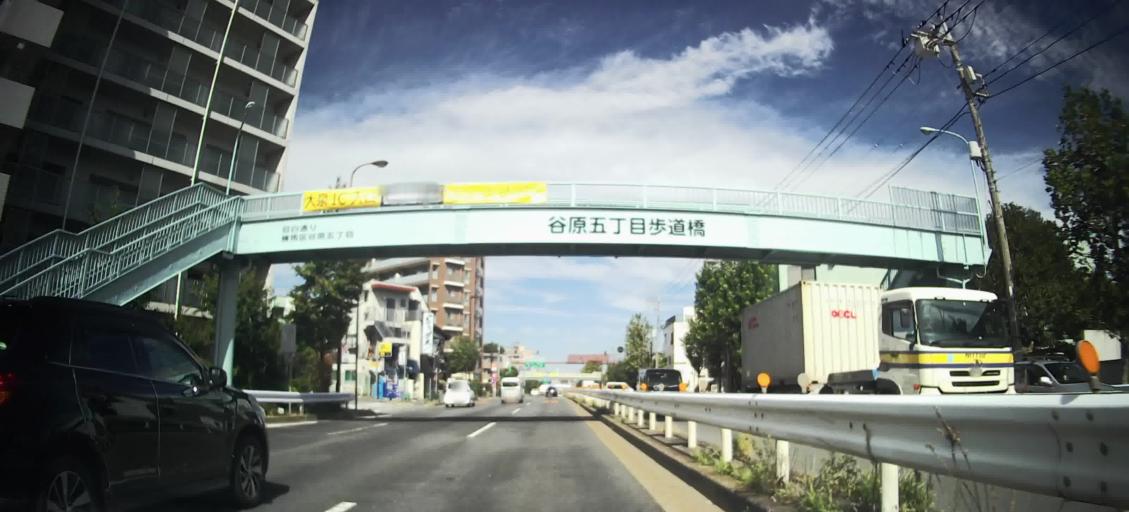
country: JP
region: Saitama
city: Wako
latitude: 35.7518
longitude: 139.6106
